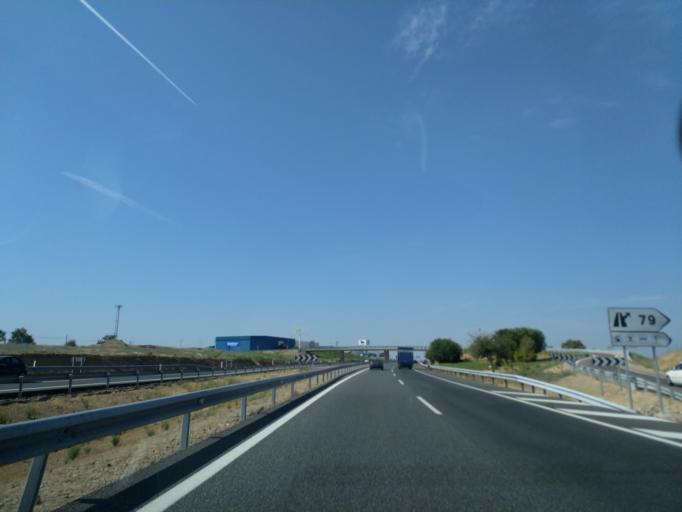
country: ES
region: Castille-La Mancha
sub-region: Province of Toledo
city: Santa Olalla
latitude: 40.0375
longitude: -4.4117
